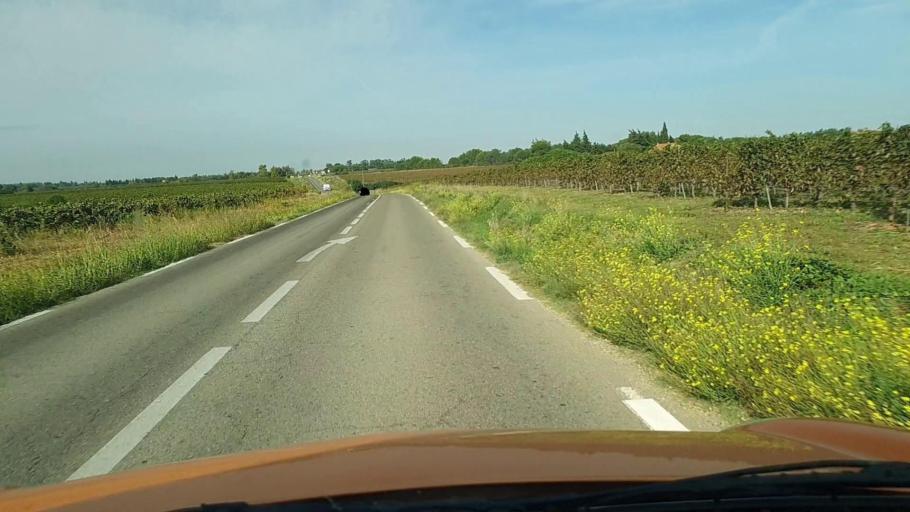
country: FR
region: Languedoc-Roussillon
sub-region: Departement du Gard
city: Vauvert
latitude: 43.6518
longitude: 4.3099
